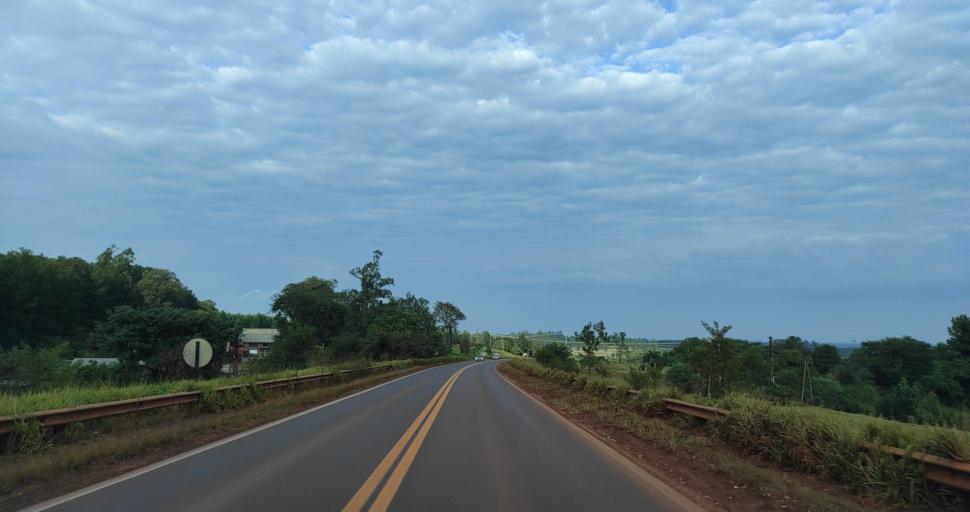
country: AR
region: Corrientes
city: Gobernador Ingeniero Valentin Virasoro
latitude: -27.9511
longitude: -55.9935
